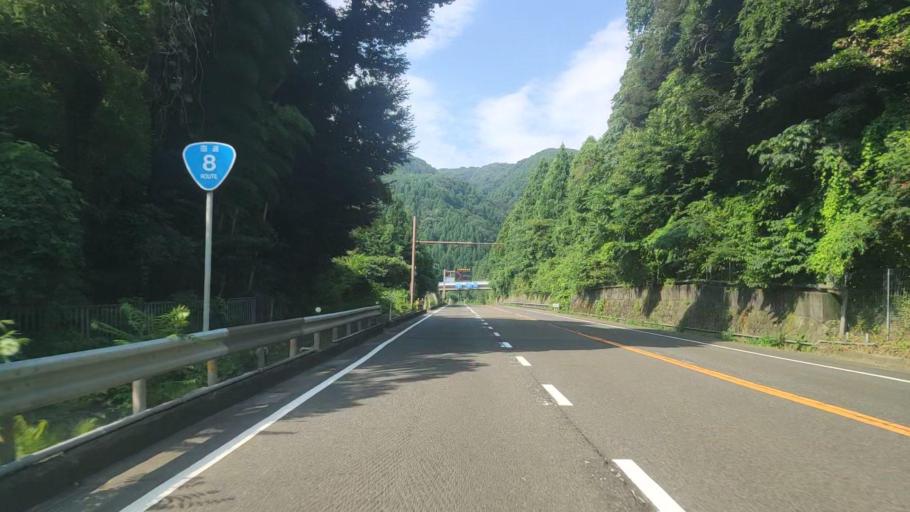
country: JP
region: Fukui
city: Tsuruga
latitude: 35.7535
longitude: 136.1043
